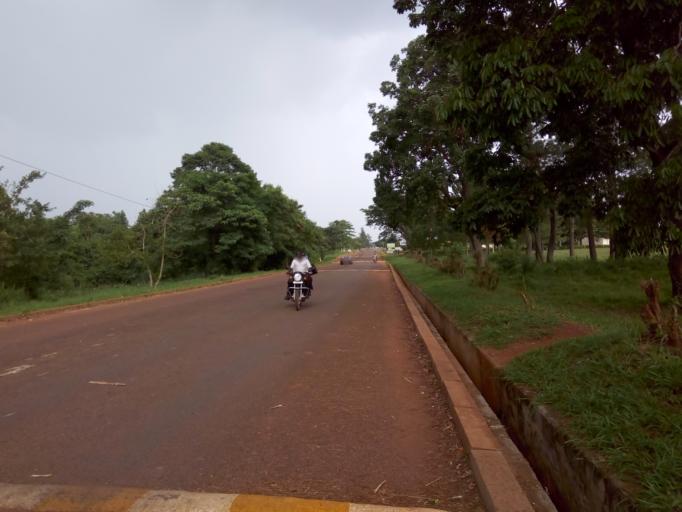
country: UG
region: Western Region
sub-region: Masindi District
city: Masindi
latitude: 1.6843
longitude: 31.7045
